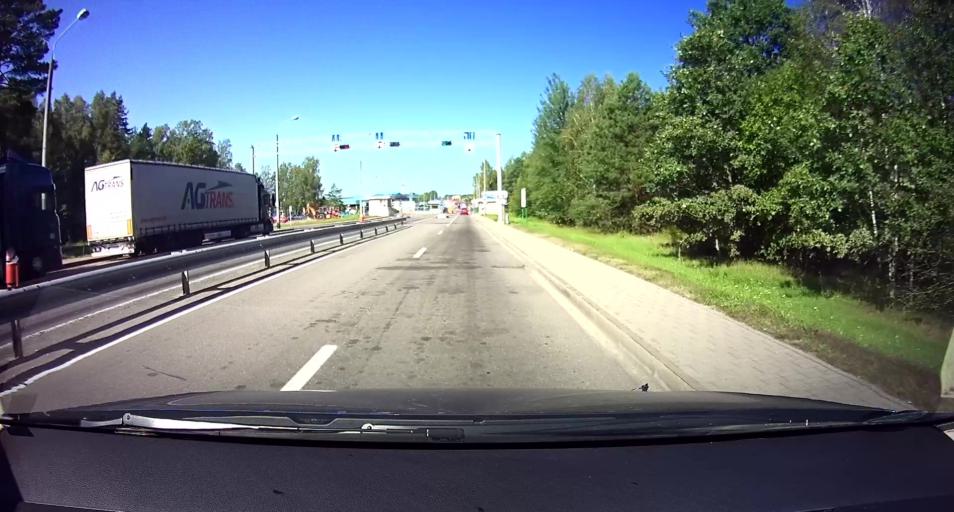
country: BY
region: Grodnenskaya
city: Vyalikaya Byerastavitsa
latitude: 53.1222
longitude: 23.9027
